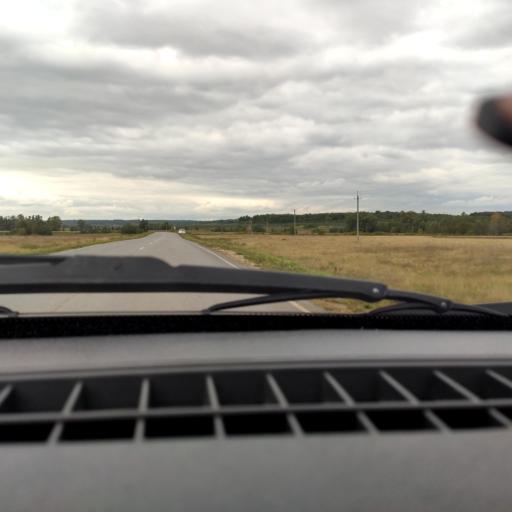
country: RU
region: Bashkortostan
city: Iglino
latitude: 54.7237
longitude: 56.4049
